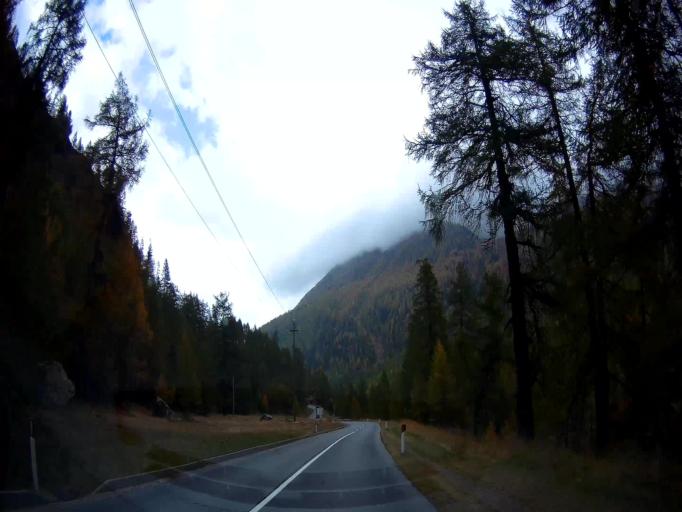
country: IT
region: Trentino-Alto Adige
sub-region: Bolzano
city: Senales
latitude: 46.7326
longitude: 10.8092
